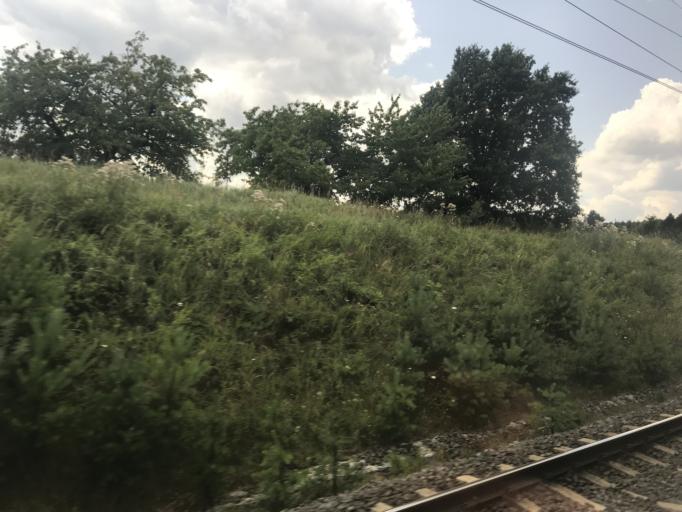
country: PL
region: Lubusz
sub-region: Powiat sulecinski
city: Torzym
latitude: 52.3196
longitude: 15.0220
